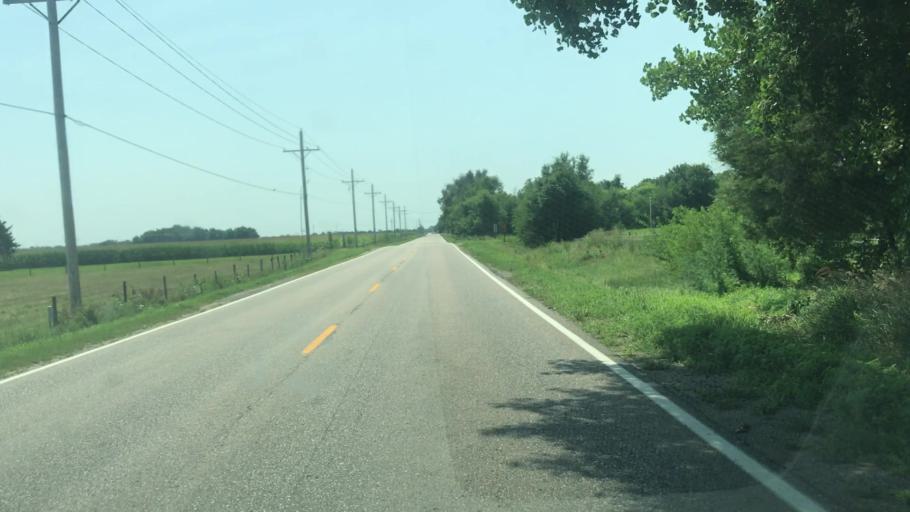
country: US
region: Nebraska
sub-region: Hall County
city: Grand Island
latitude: 40.8925
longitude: -98.3017
